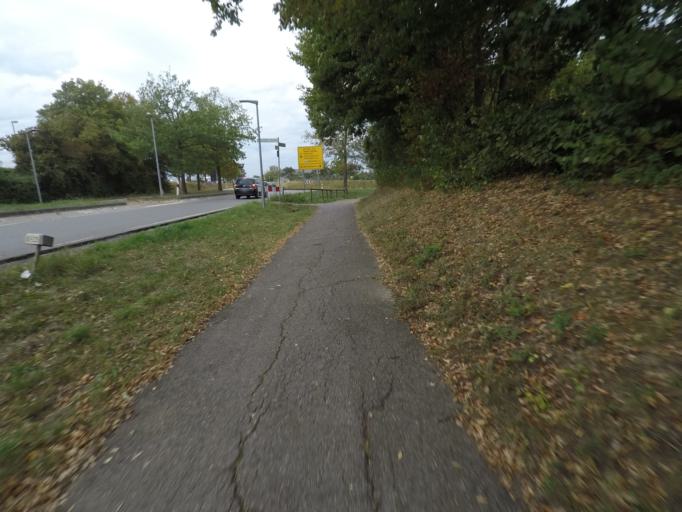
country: DE
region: Baden-Wuerttemberg
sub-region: Regierungsbezirk Stuttgart
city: Filderstadt
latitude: 48.6519
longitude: 9.2313
